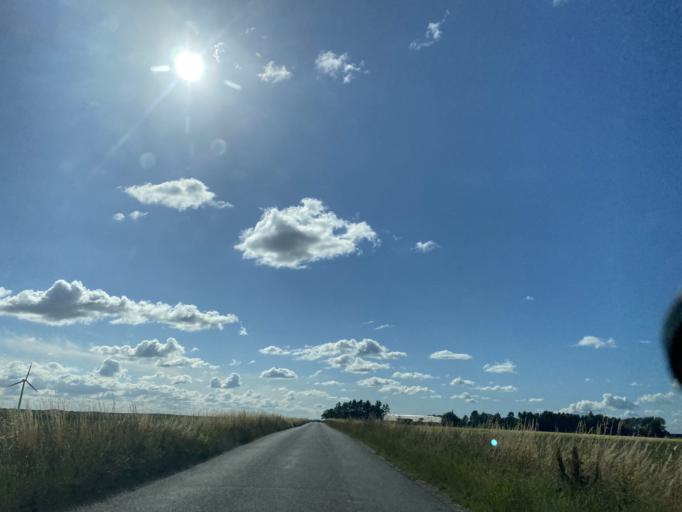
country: DK
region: Central Jutland
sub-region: Viborg Kommune
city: Bjerringbro
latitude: 56.3380
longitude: 9.7068
